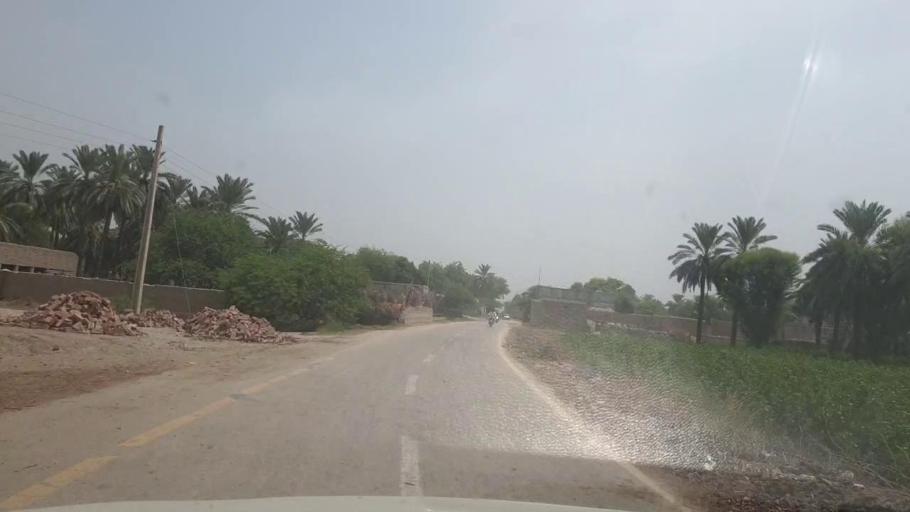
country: PK
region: Sindh
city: Kot Diji
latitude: 27.3712
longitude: 68.6483
